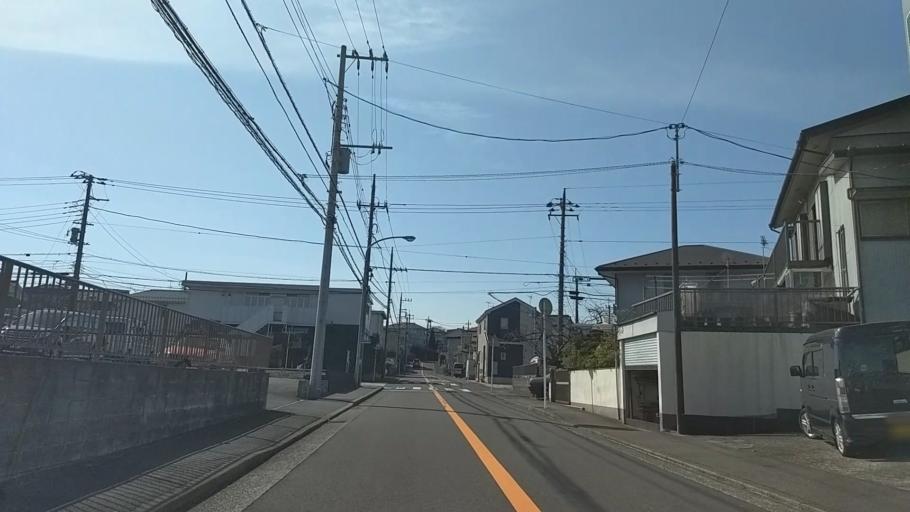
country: JP
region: Kanagawa
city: Kamakura
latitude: 35.3916
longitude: 139.5557
